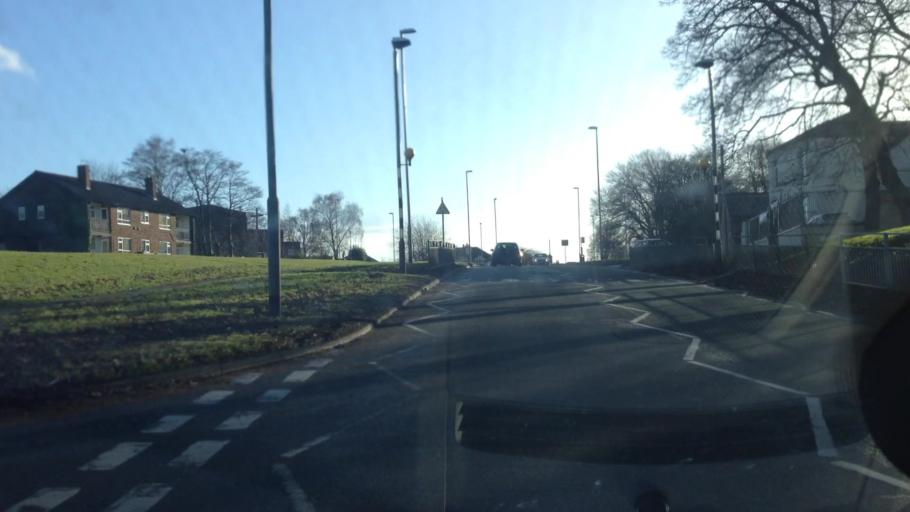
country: GB
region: England
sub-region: City and Borough of Leeds
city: Chapel Allerton
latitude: 53.8444
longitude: -1.5468
